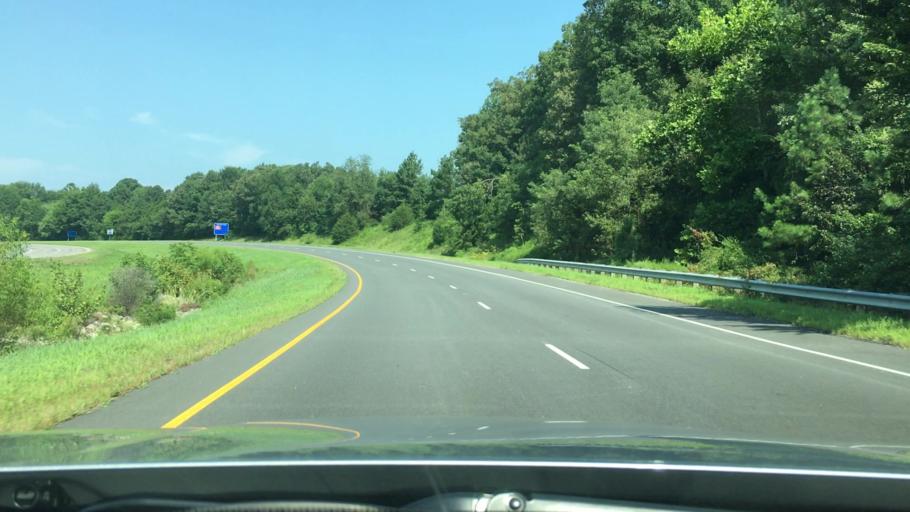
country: US
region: Virginia
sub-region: Caroline County
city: Bowling Green
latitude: 38.0386
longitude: -77.3561
